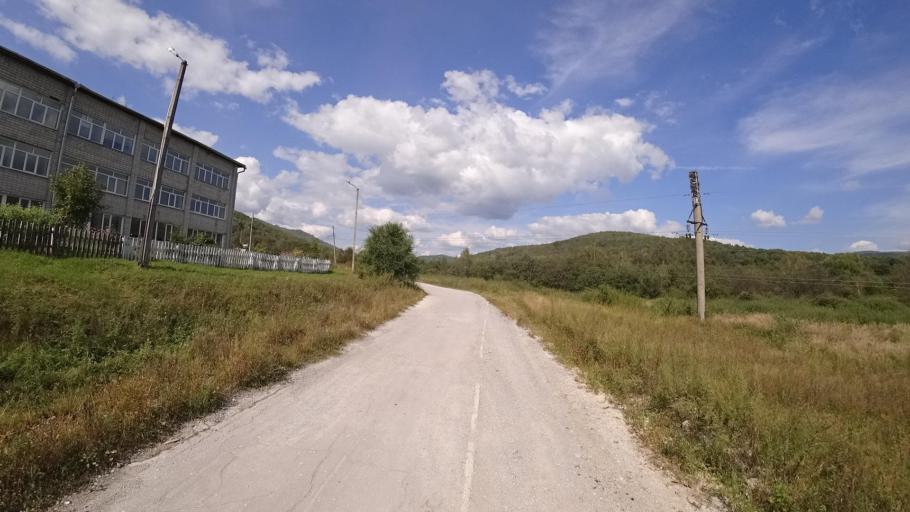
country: RU
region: Jewish Autonomous Oblast
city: Londoko
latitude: 49.0271
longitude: 131.9262
